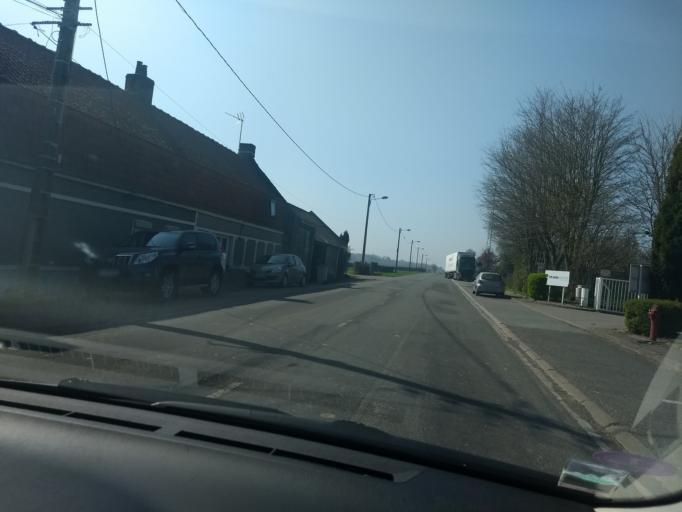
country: FR
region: Nord-Pas-de-Calais
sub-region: Departement du Pas-de-Calais
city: Tatinghem
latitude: 50.7386
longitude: 2.1993
